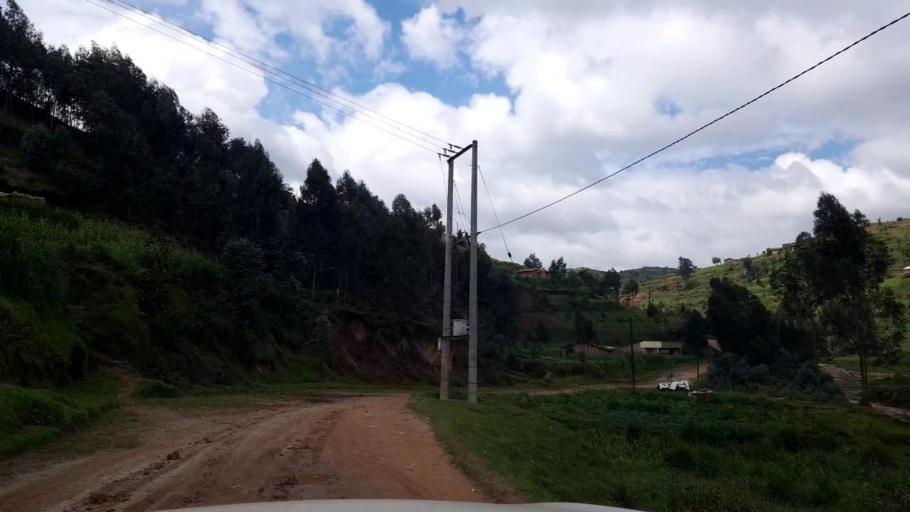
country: RW
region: Western Province
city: Kibuye
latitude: -1.9129
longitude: 29.4568
